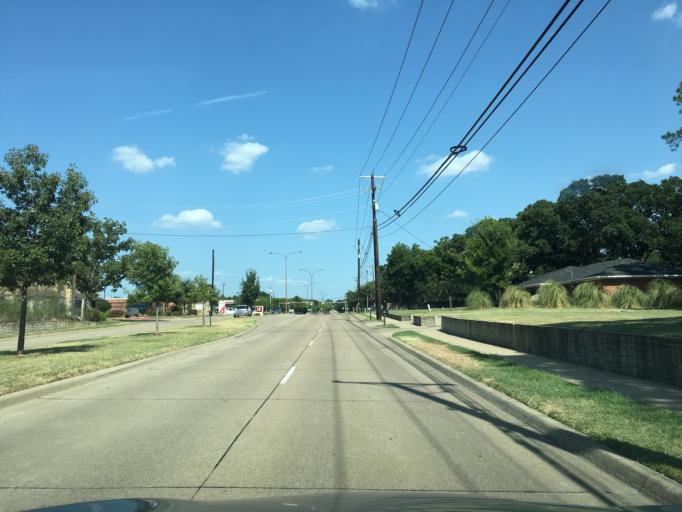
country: US
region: Texas
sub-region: Tarrant County
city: Dalworthington Gardens
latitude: 32.6777
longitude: -97.1524
